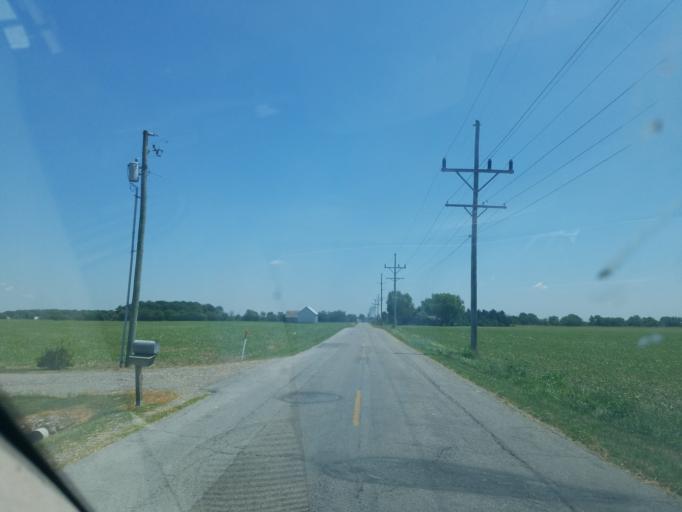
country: US
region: Ohio
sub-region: Allen County
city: Delphos
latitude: 40.7795
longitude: -84.3470
